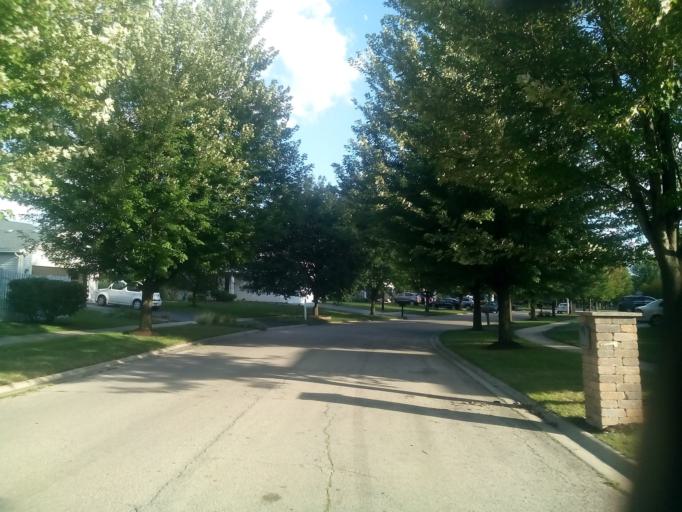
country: US
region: Illinois
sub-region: Will County
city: Romeoville
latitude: 41.6938
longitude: -88.1516
